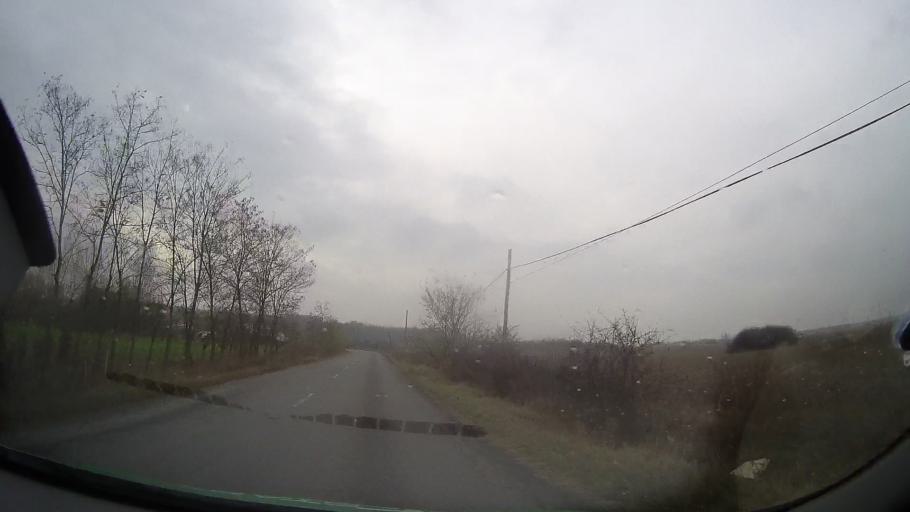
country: RO
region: Prahova
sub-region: Comuna Gherghita
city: Gherghita
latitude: 44.8177
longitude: 26.2693
